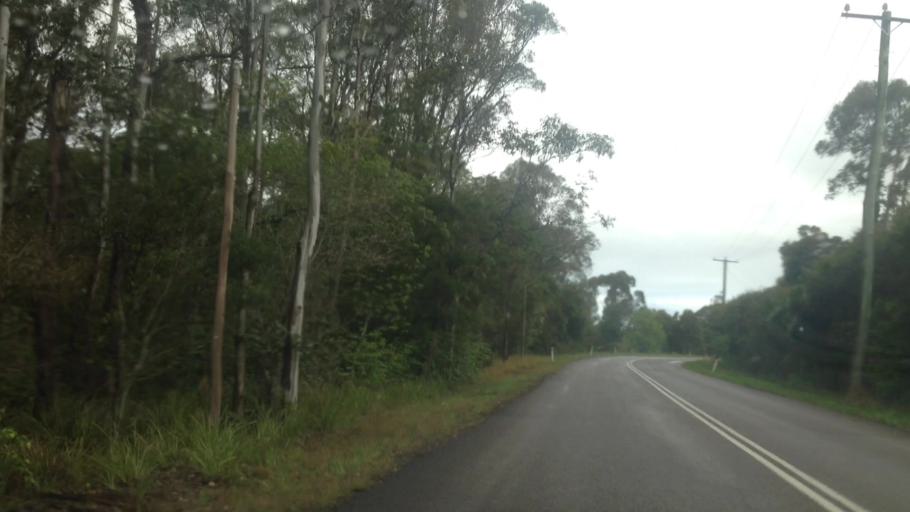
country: AU
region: New South Wales
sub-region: Wyong Shire
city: Little Jilliby
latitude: -33.2533
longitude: 151.3834
